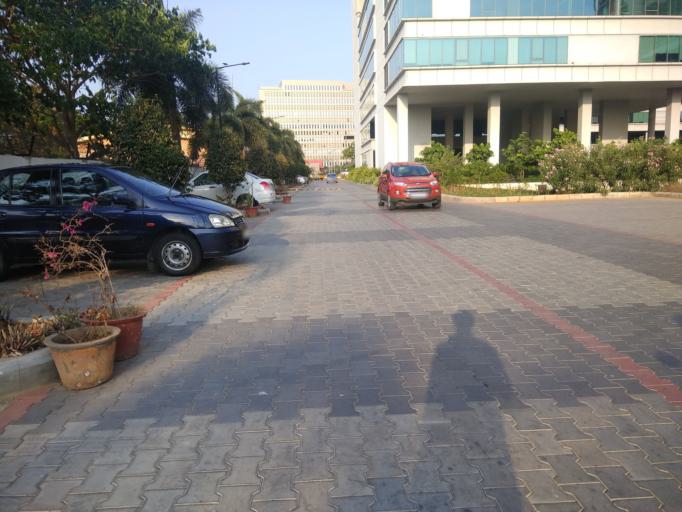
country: IN
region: Tamil Nadu
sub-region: Chennai
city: Gandhi Nagar
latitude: 12.9915
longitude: 80.2424
